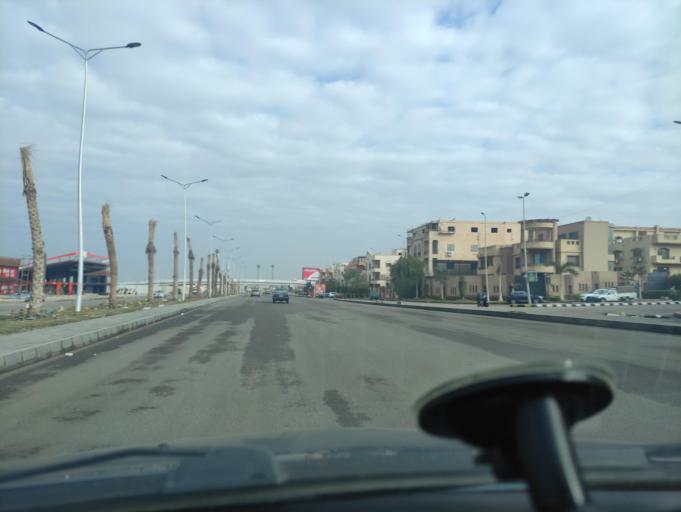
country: EG
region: Muhafazat al Qalyubiyah
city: Al Khankah
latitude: 30.0481
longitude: 31.4426
